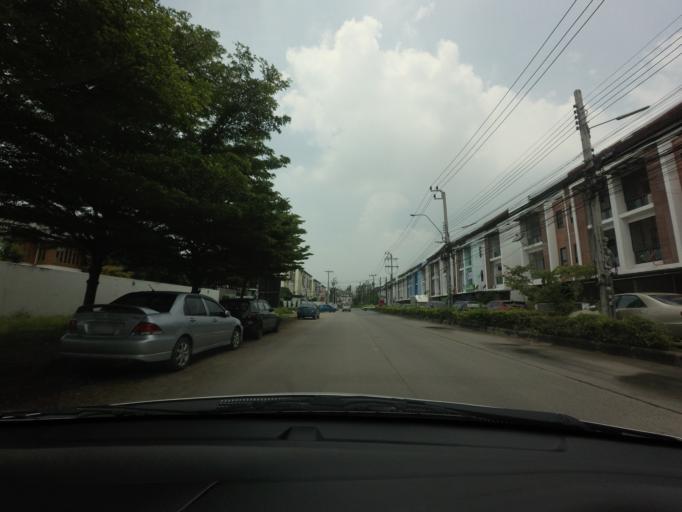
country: TH
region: Bangkok
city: Bang Na
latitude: 13.6639
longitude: 100.6917
